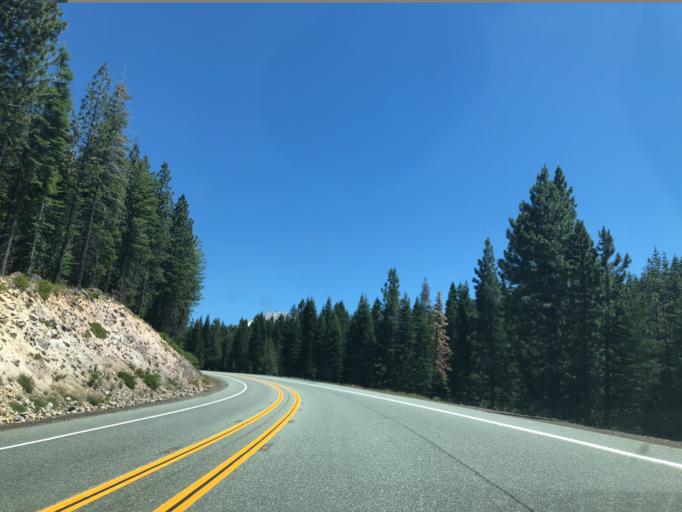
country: US
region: California
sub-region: Shasta County
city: Shingletown
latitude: 40.5398
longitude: -121.5983
